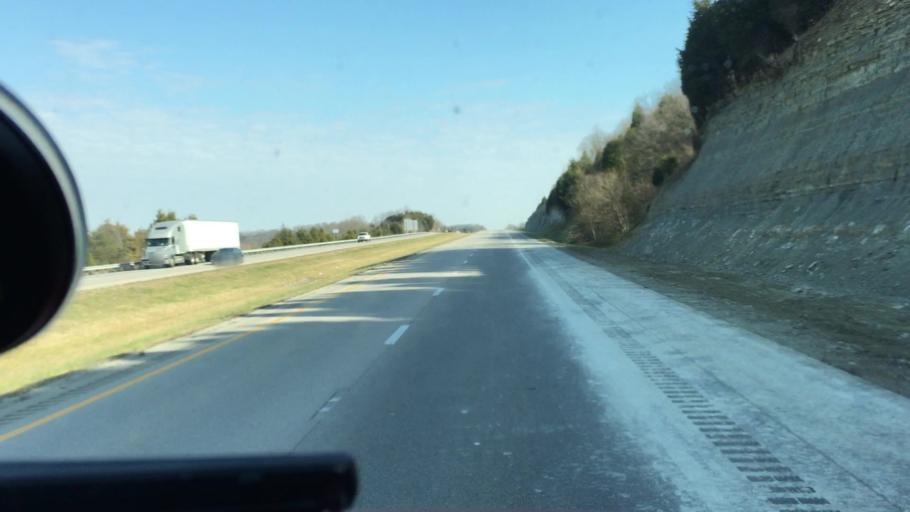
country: US
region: Kentucky
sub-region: Bath County
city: Owingsville
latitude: 38.1336
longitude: -83.7360
